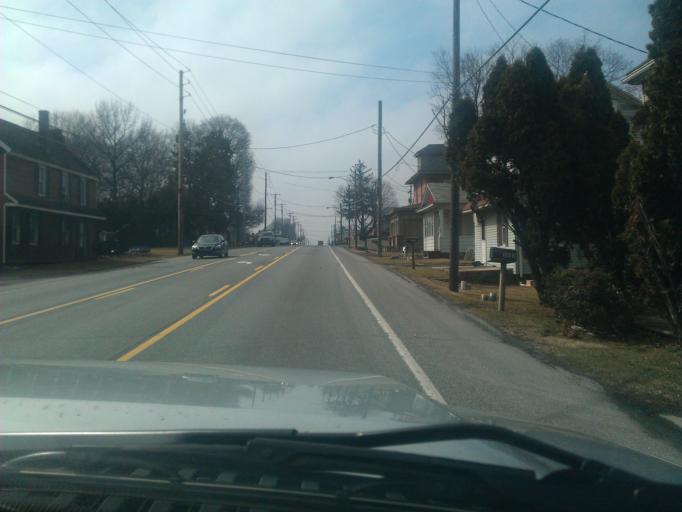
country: US
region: Pennsylvania
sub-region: Lancaster County
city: Paradise
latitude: 40.0152
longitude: -76.1558
